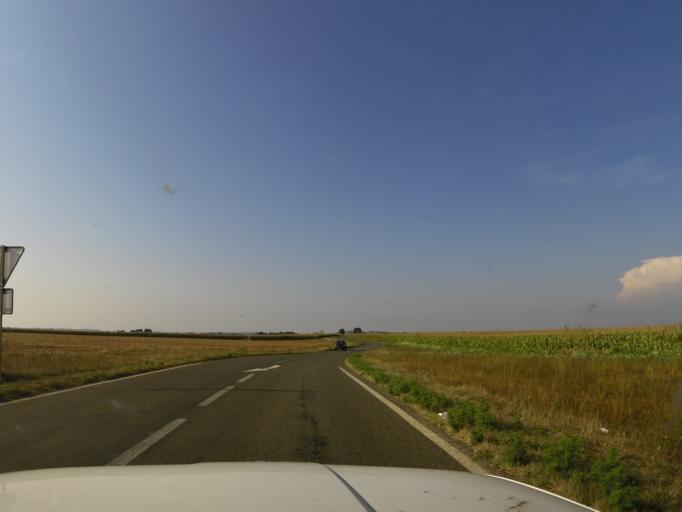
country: FR
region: Rhone-Alpes
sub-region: Departement de l'Ain
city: Chazey-sur-Ain
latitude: 45.8586
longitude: 5.2485
